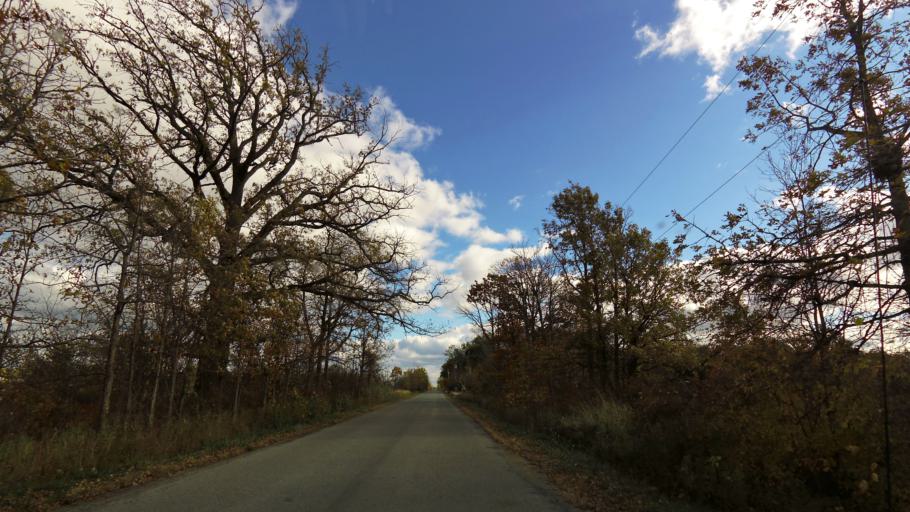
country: CA
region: Ontario
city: Burlington
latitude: 43.4491
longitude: -79.8554
